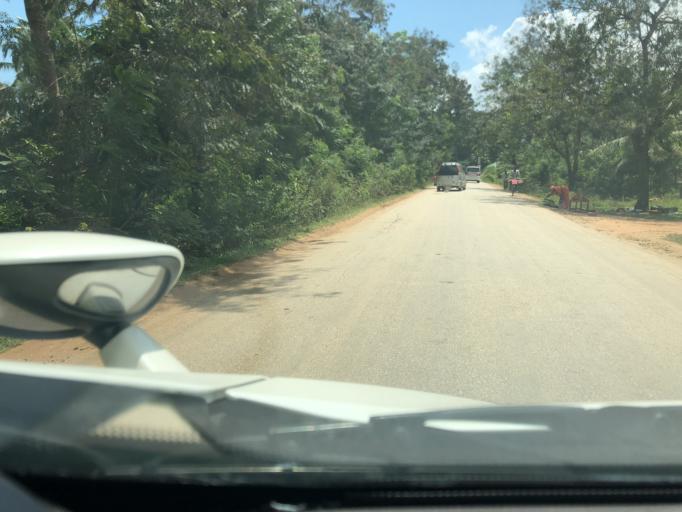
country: TZ
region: Zanzibar Central/South
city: Koani
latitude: -6.0606
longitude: 39.2521
